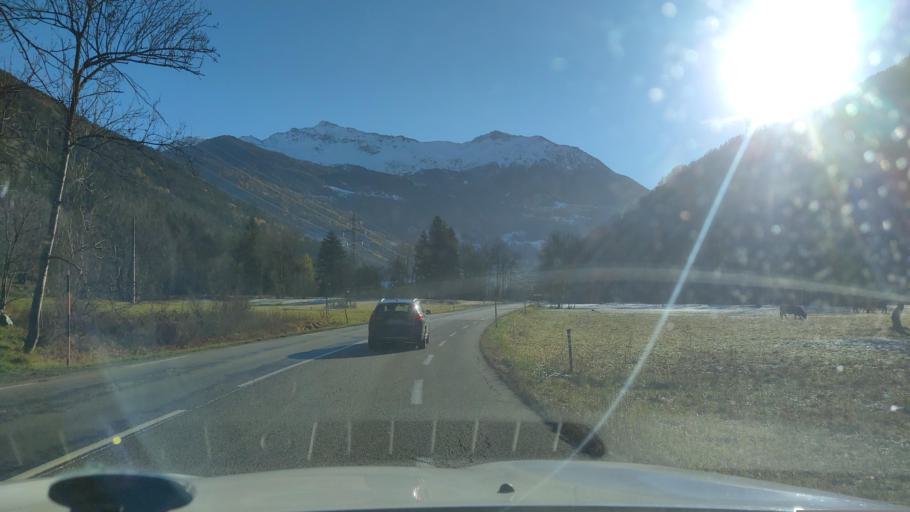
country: FR
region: Rhone-Alpes
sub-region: Departement de la Savoie
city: Seez
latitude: 45.6057
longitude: 6.8547
